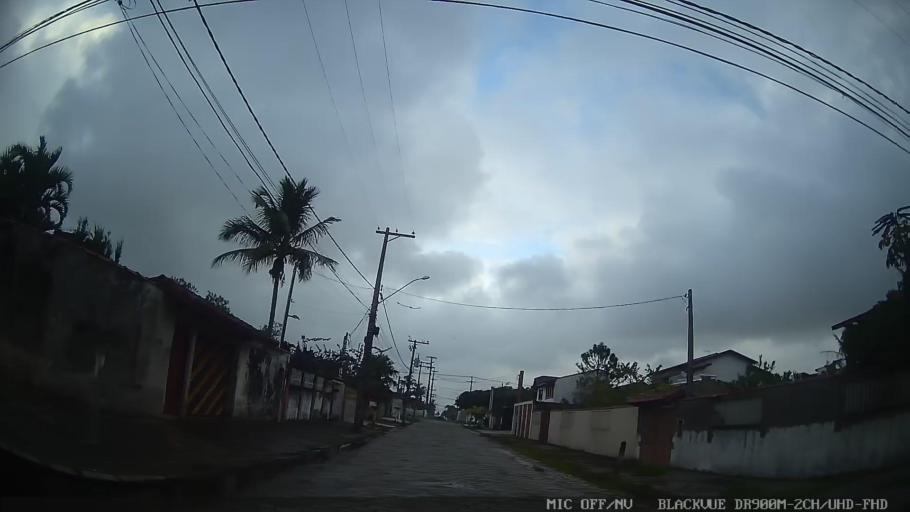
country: BR
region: Sao Paulo
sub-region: Itanhaem
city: Itanhaem
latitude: -24.2030
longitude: -46.8312
